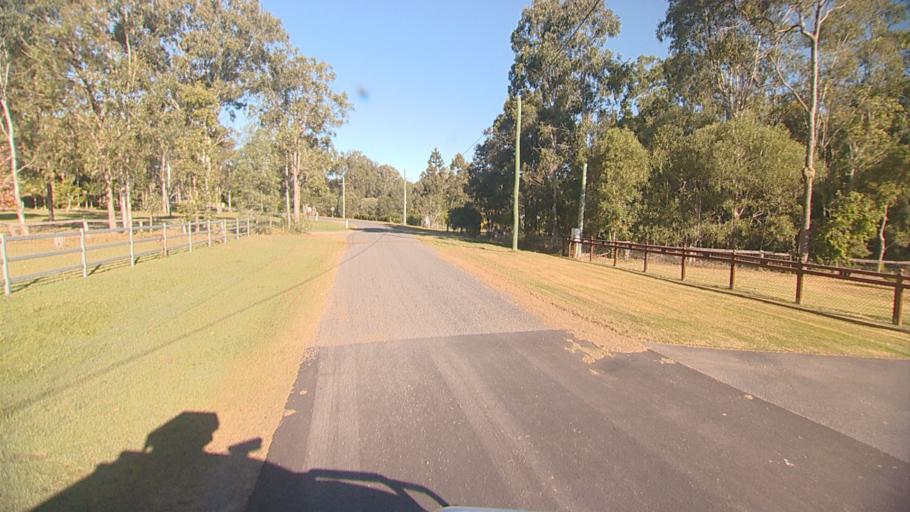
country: AU
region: Queensland
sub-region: Logan
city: Logan Reserve
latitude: -27.7437
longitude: 153.1054
